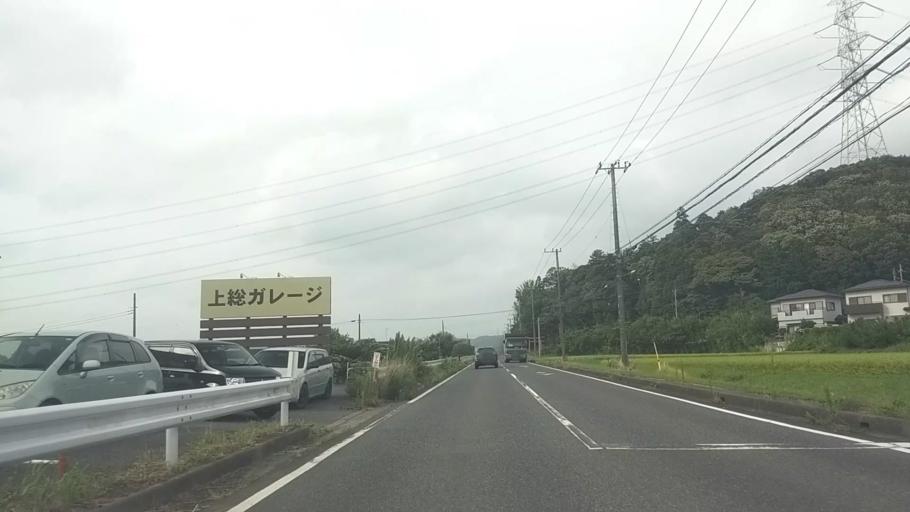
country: JP
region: Chiba
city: Kimitsu
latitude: 35.2826
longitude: 139.9901
